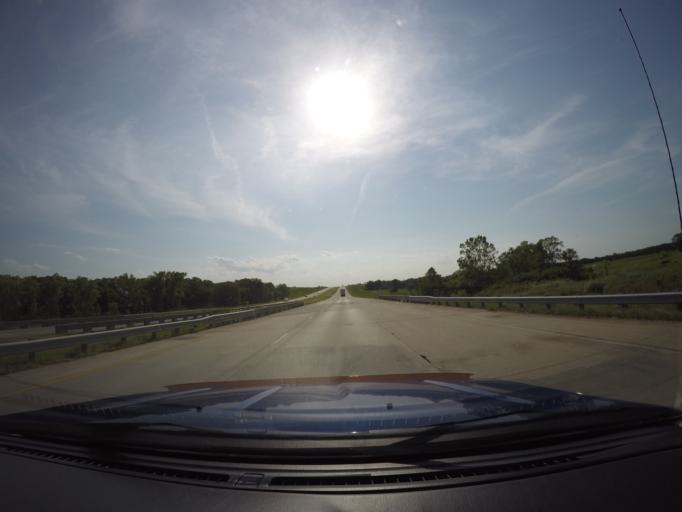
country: US
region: Kansas
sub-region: Wabaunsee County
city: Alma
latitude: 39.0656
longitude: -96.3587
